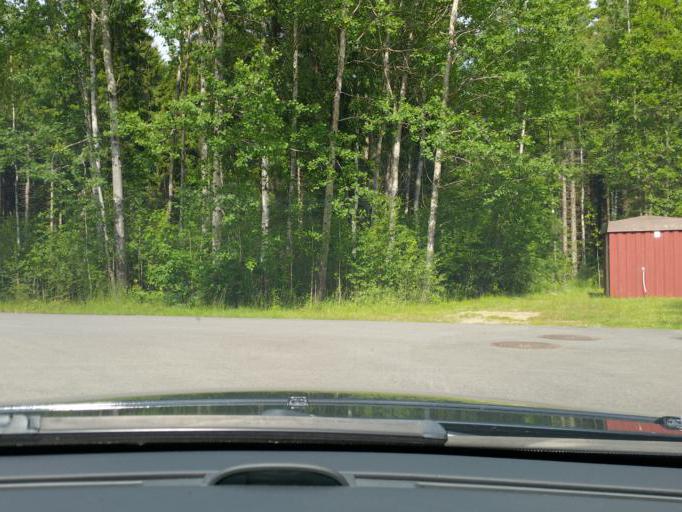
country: SE
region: Kronoberg
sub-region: Vaxjo Kommun
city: Lammhult
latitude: 57.1717
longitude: 14.6080
